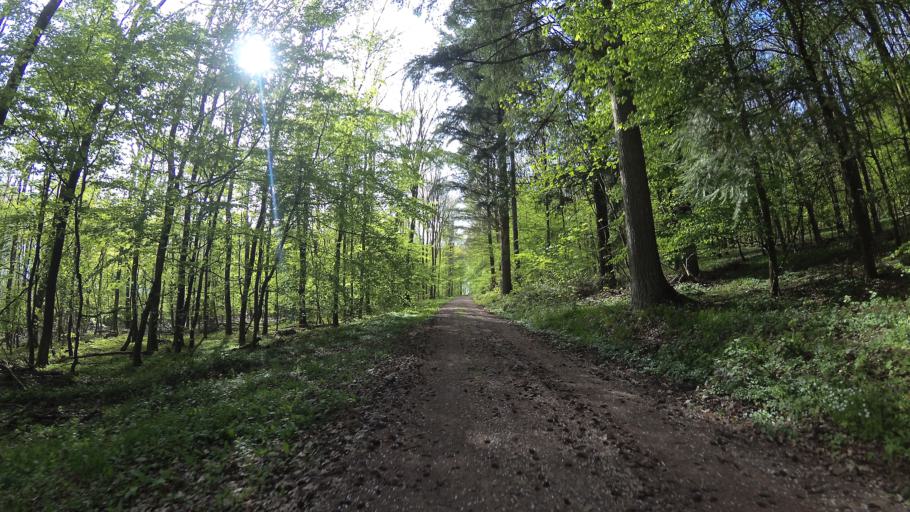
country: DE
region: Saarland
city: Mainzweiler
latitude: 49.4437
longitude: 7.1384
